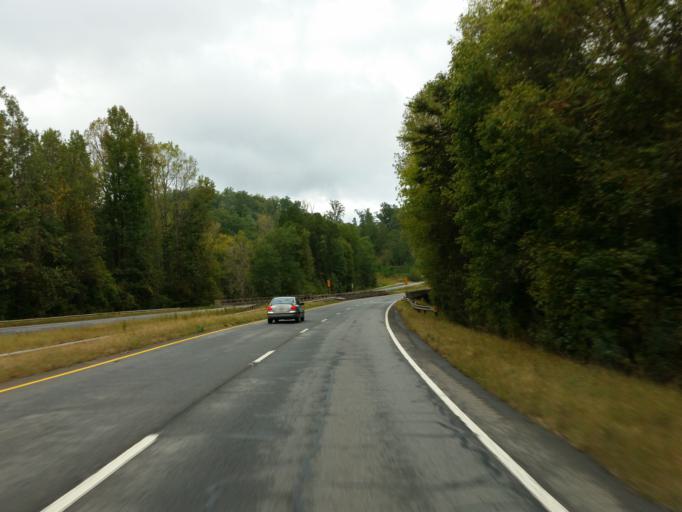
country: US
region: Georgia
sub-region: Bartow County
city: Emerson
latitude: 34.1097
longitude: -84.7498
